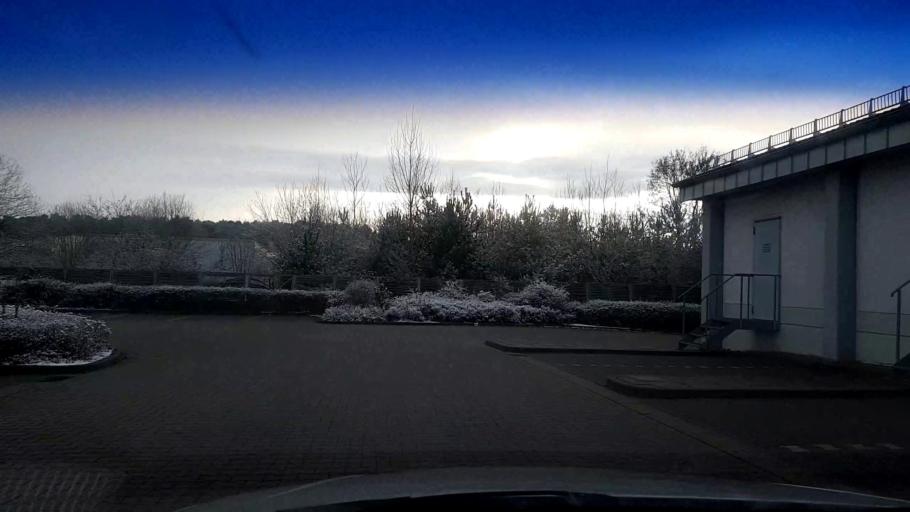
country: DE
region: Bavaria
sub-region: Upper Franconia
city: Hirschaid
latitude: 49.8293
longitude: 10.9871
